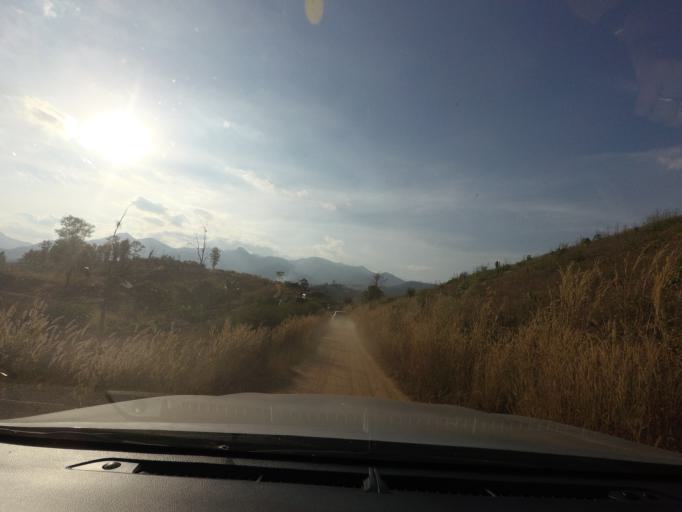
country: TH
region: Mae Hong Son
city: Wiang Nuea
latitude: 19.4008
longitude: 98.4075
